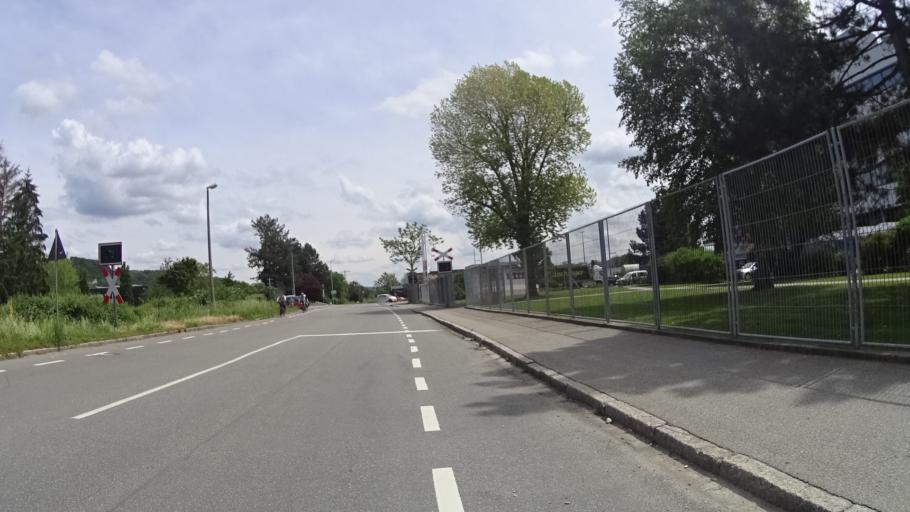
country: DE
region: Baden-Wuerttemberg
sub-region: Freiburg Region
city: Grenzach-Wyhlen
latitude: 47.5496
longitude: 7.6676
